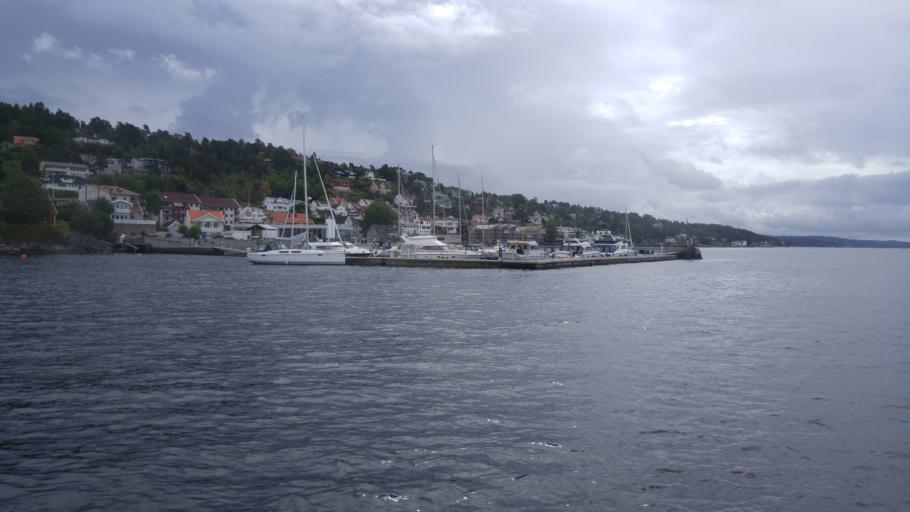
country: NO
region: Akershus
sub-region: Frogn
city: Drobak
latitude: 59.6602
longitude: 10.6259
